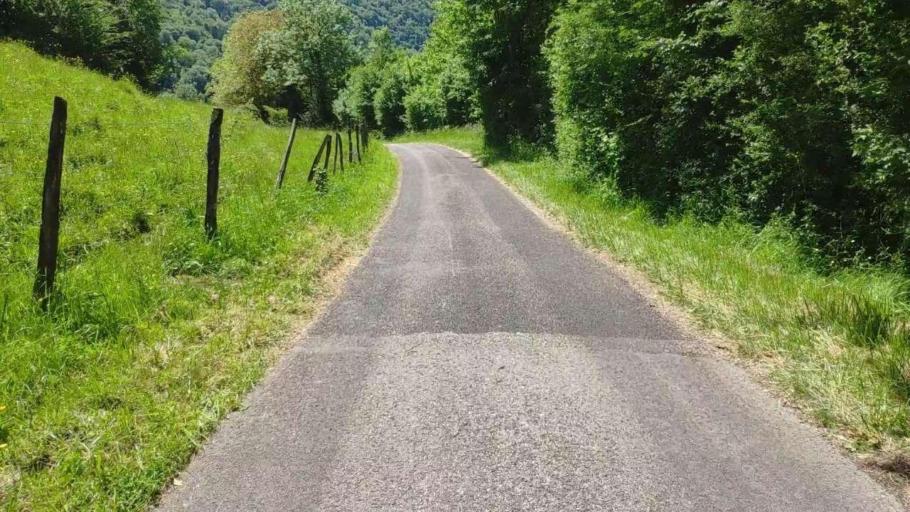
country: FR
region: Franche-Comte
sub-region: Departement du Jura
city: Poligny
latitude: 46.7538
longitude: 5.6747
